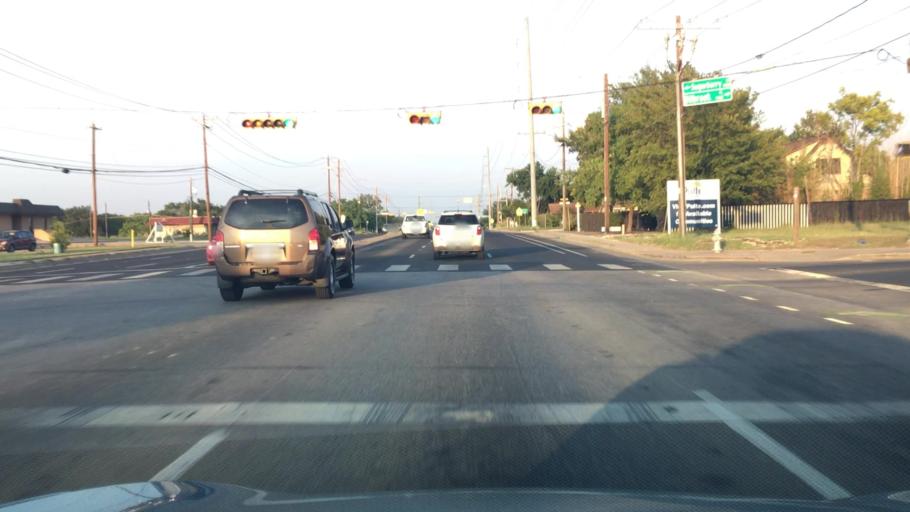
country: US
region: Texas
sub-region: Travis County
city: Manchaca
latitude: 30.1738
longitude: -97.8171
